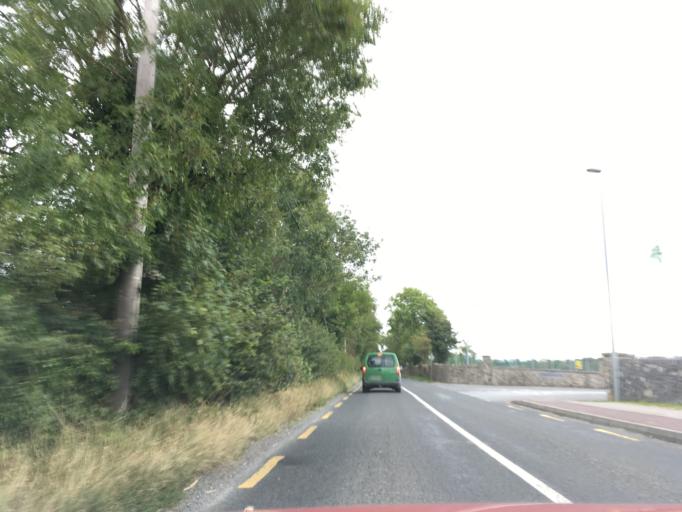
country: IE
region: Munster
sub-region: South Tipperary
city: Cluain Meala
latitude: 52.4105
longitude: -7.7488
